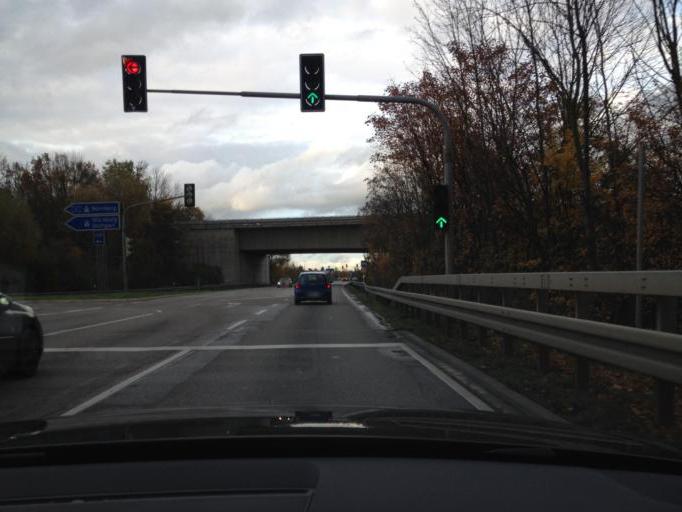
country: DE
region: Baden-Wuerttemberg
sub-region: Regierungsbezirk Stuttgart
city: Neckarsulm
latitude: 49.1846
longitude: 9.2018
